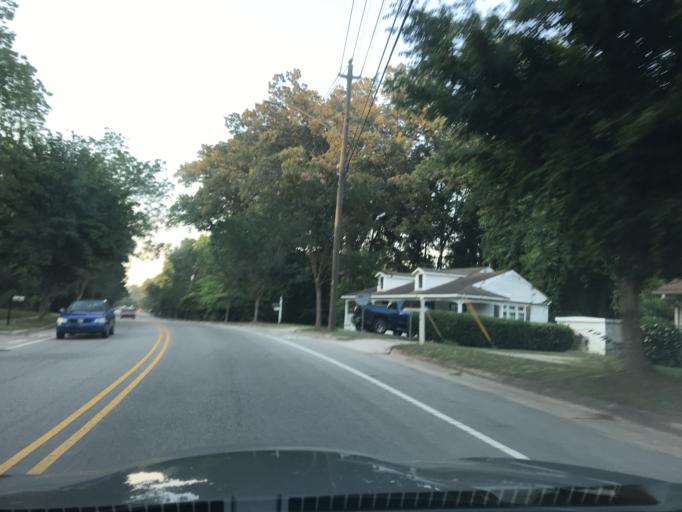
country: US
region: North Carolina
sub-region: Wake County
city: Raleigh
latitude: 35.7484
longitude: -78.6192
